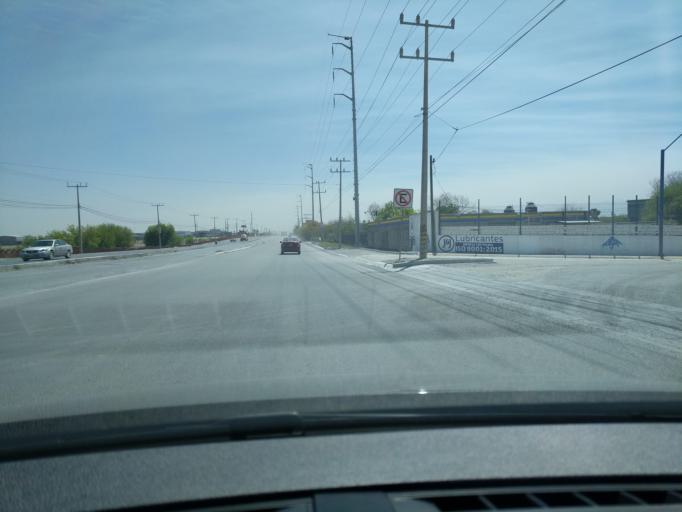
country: MX
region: Nuevo Leon
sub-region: Salinas Victoria
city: Emiliano Zapata
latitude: 25.8973
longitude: -100.2615
